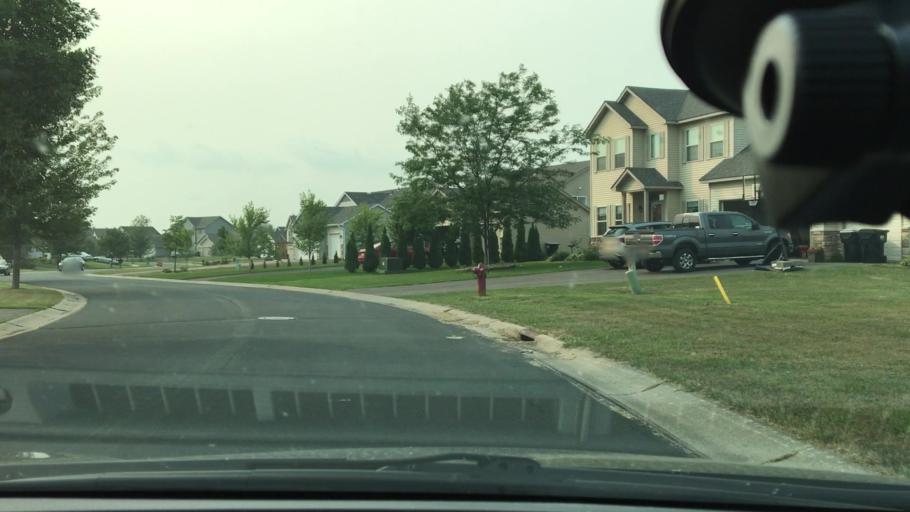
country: US
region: Minnesota
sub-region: Wright County
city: Albertville
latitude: 45.2540
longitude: -93.6533
